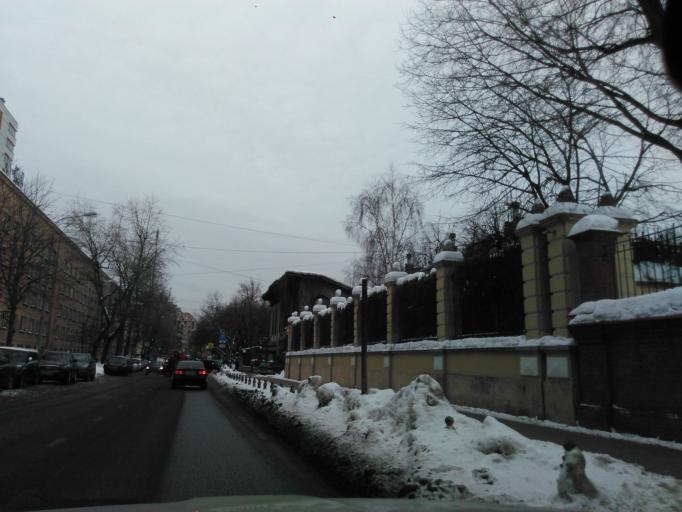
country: RU
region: Moskovskaya
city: Dorogomilovo
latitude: 55.7667
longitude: 37.5722
